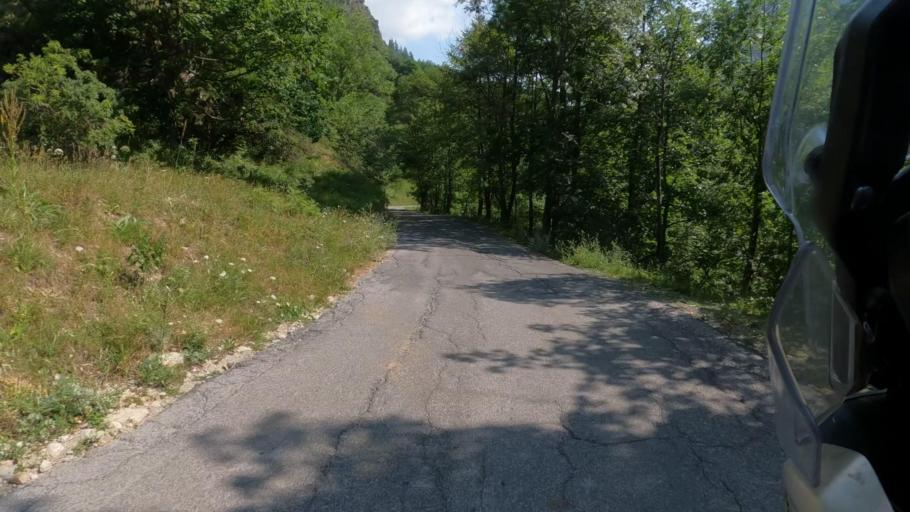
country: IT
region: Piedmont
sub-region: Provincia di Cuneo
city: Canosio
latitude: 44.4419
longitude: 7.0599
